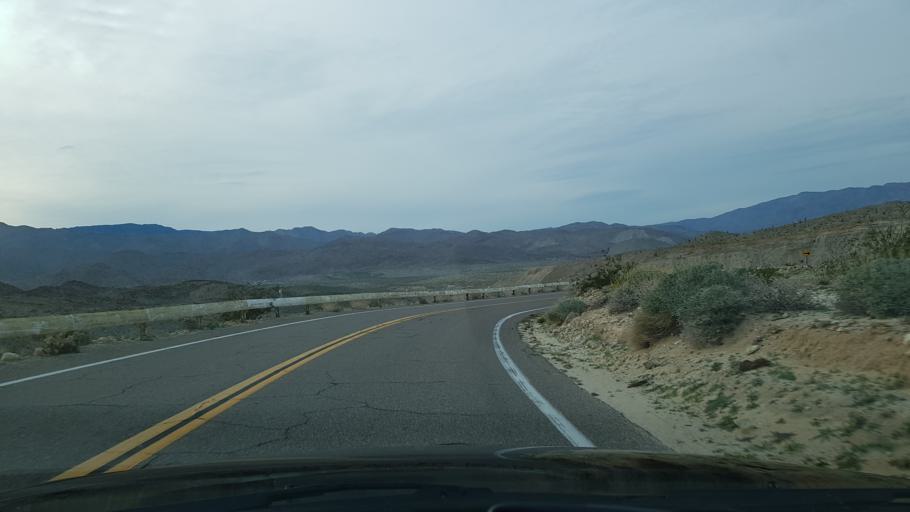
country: US
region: California
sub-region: San Diego County
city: Pine Valley
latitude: 32.8320
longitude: -116.1811
